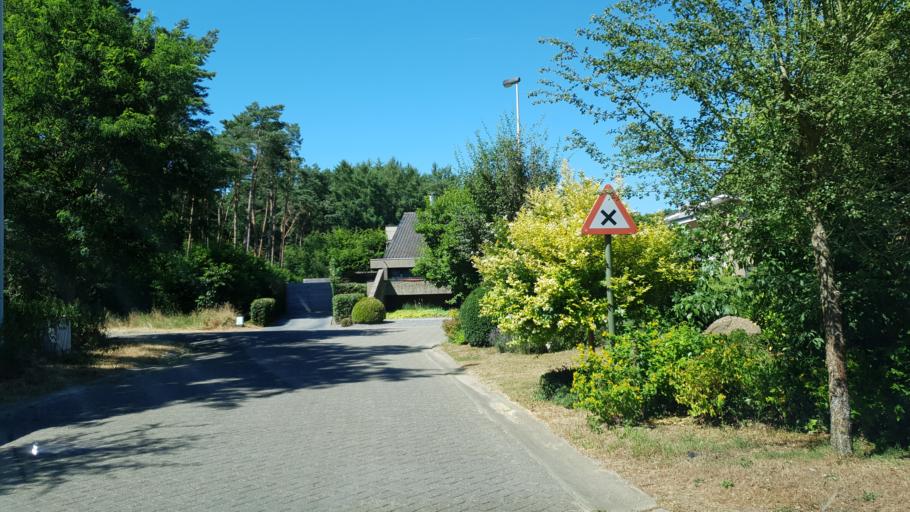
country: BE
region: Flanders
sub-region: Provincie Antwerpen
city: Grobbendonk
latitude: 51.1971
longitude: 4.7409
